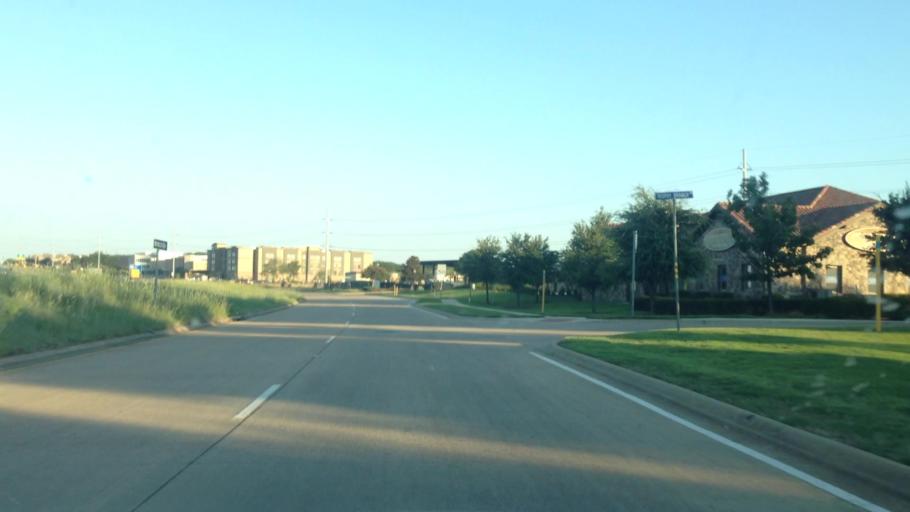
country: US
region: Texas
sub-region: Denton County
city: Trophy Club
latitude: 32.9852
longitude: -97.1695
